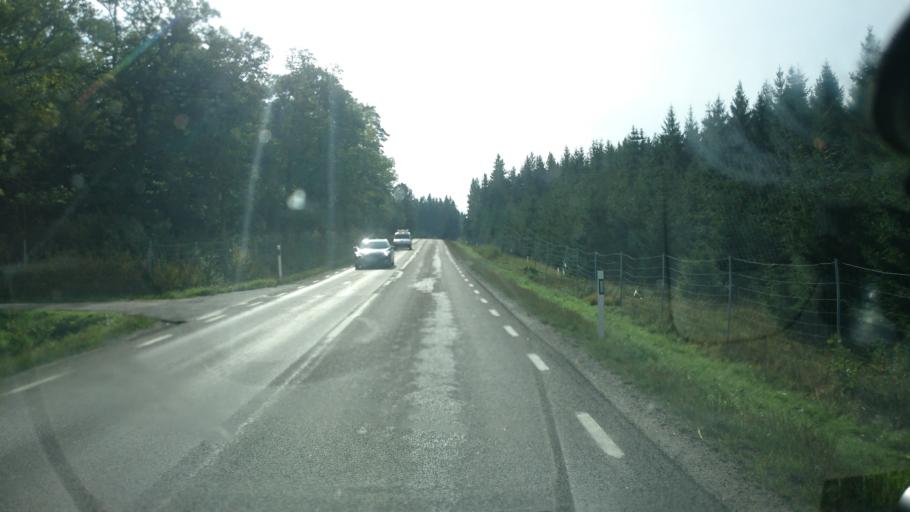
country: SE
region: Vaestra Goetaland
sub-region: Alingsas Kommun
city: Sollebrunn
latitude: 58.1472
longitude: 12.4177
